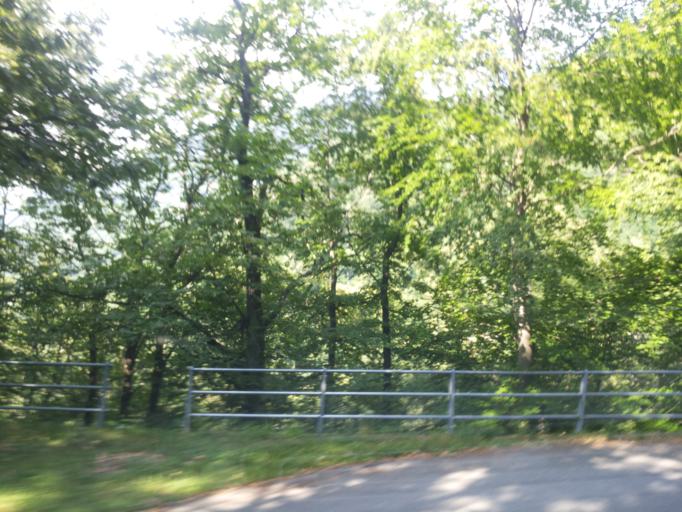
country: IT
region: Aosta Valley
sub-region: Valle d'Aosta
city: Fontainemore
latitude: 45.6474
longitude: 7.8646
